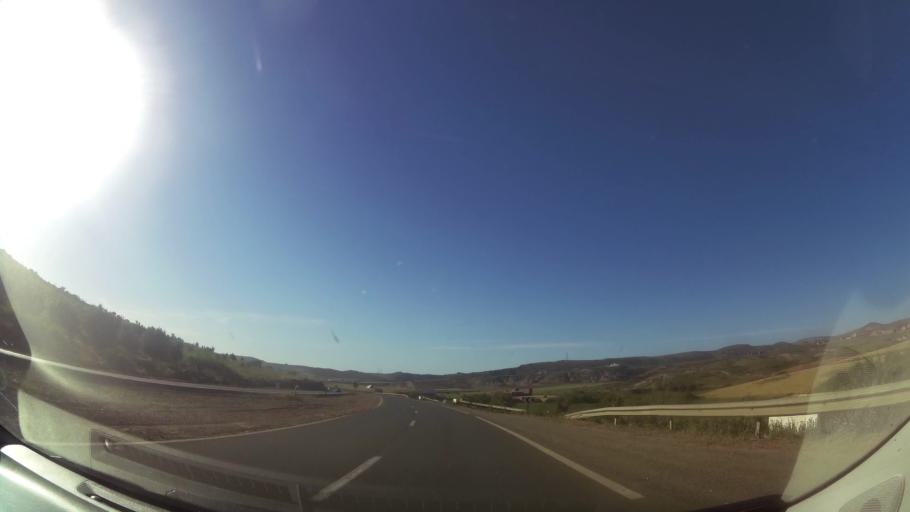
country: MA
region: Oriental
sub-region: Berkane-Taourirt
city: Ahfir
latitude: 35.0337
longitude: -2.2032
